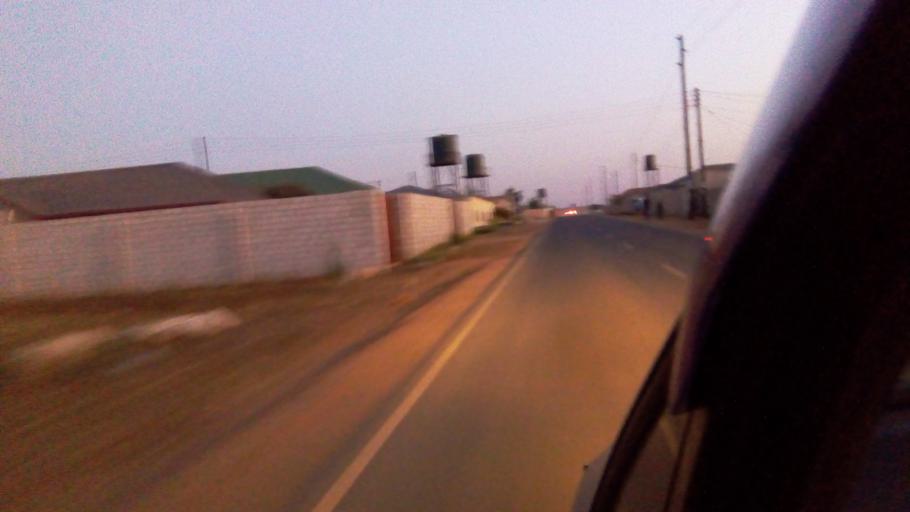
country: ZM
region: Lusaka
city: Lusaka
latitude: -15.4742
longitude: 28.3462
